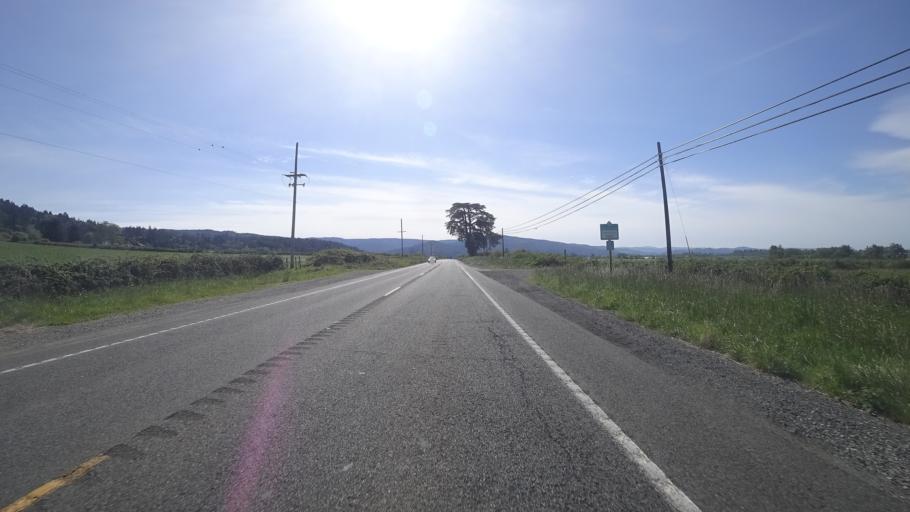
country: US
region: Oregon
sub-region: Curry County
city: Harbor
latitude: 41.9408
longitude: -124.1844
